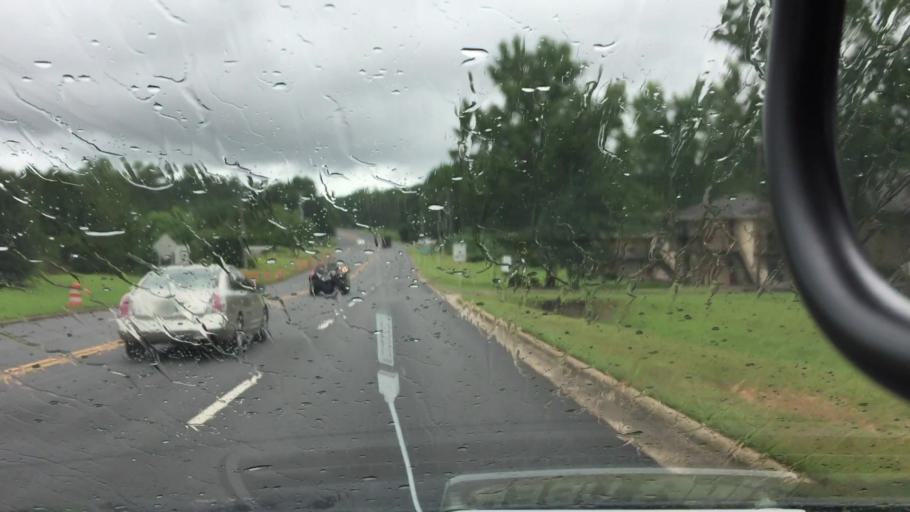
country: US
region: Alabama
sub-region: Lee County
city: Opelika
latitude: 32.6493
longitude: -85.3551
